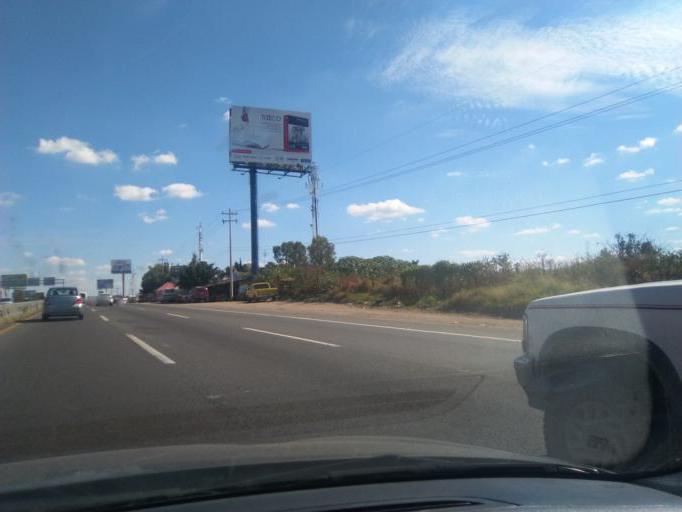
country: MX
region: Guanajuato
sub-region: Silao de la Victoria
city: El Refugio de los Sauces
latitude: 21.0404
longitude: -101.5587
